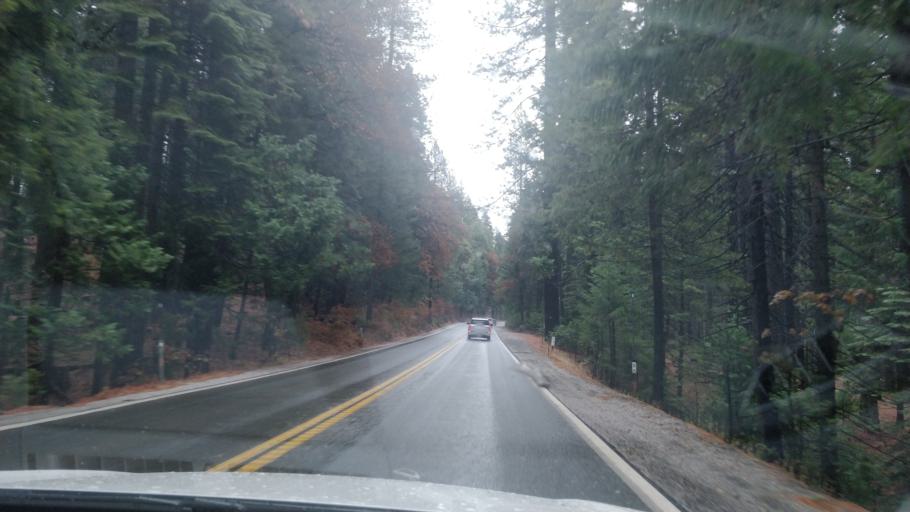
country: US
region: California
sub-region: Nevada County
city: Nevada City
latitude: 39.3215
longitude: -120.8256
